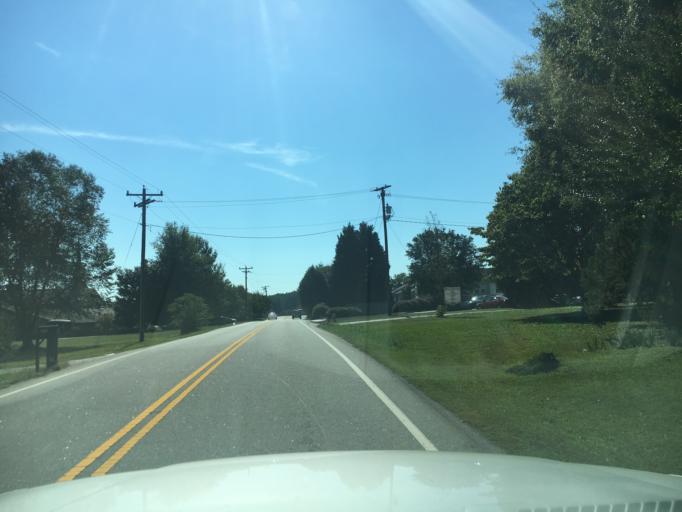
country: US
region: South Carolina
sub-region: Greenville County
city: Taylors
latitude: 34.8666
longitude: -82.2817
